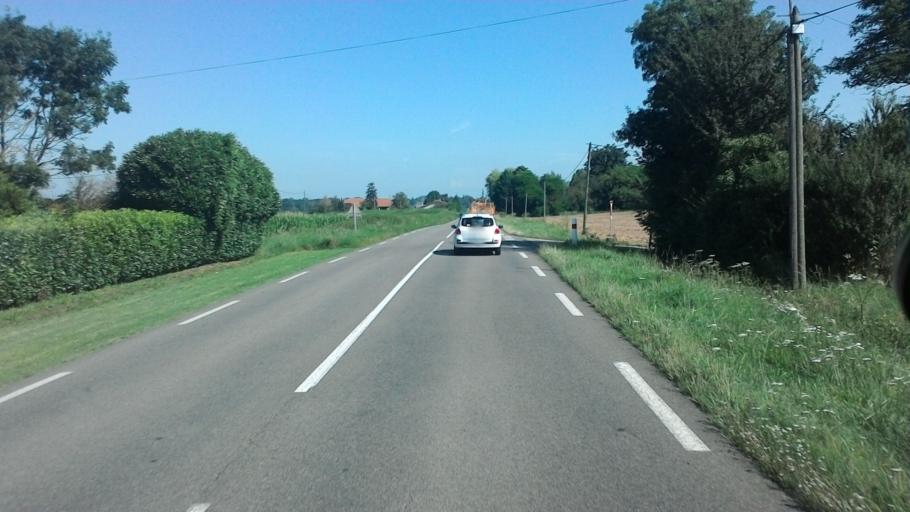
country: FR
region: Rhone-Alpes
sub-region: Departement de l'Ain
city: Saint-Trivier-de-Courtes
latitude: 46.4422
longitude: 5.0906
